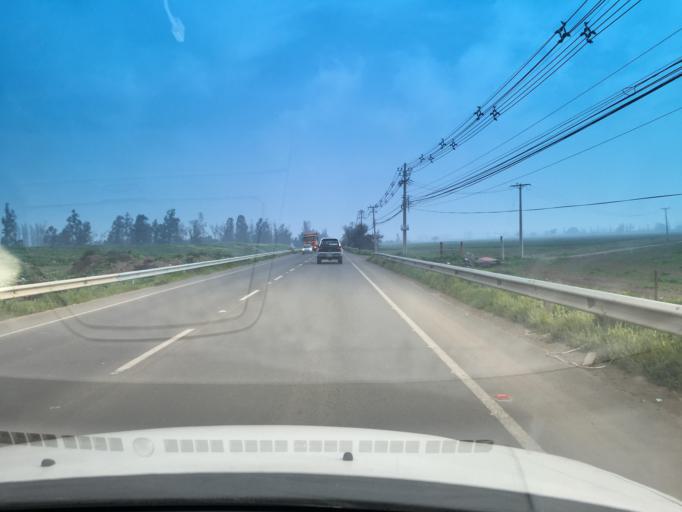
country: CL
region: Santiago Metropolitan
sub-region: Provincia de Chacabuco
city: Lampa
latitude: -33.3440
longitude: -70.8100
